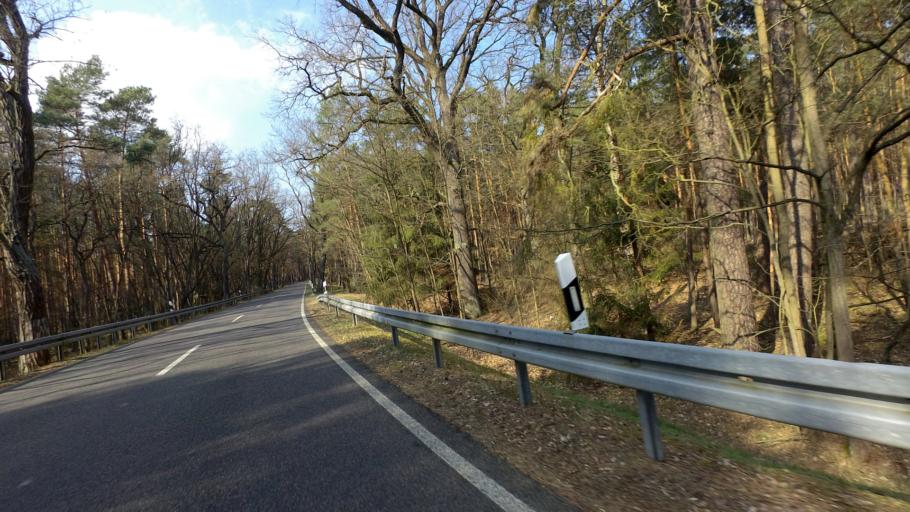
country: DE
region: Brandenburg
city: Dahme
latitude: 51.9350
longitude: 13.4475
